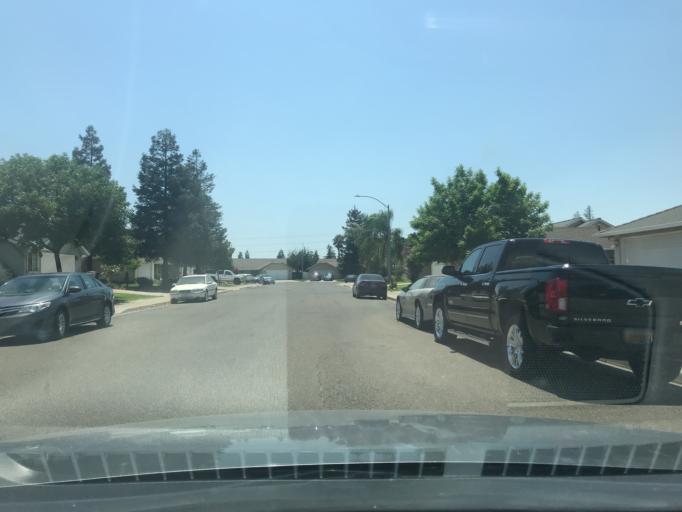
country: US
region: California
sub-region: Merced County
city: Atwater
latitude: 37.3699
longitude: -120.5922
